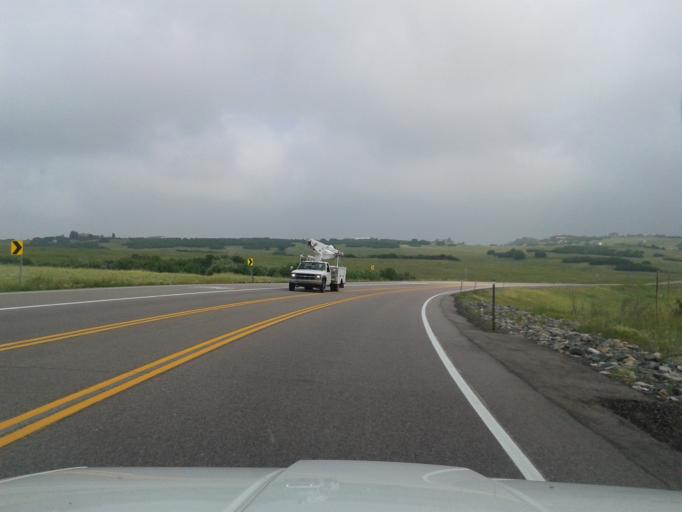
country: US
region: Colorado
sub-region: Douglas County
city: Castle Rock
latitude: 39.2714
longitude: -104.7366
